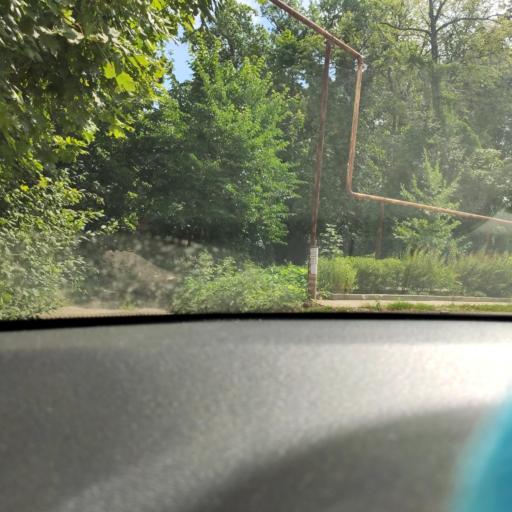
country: RU
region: Samara
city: Samara
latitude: 53.2972
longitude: 50.2334
